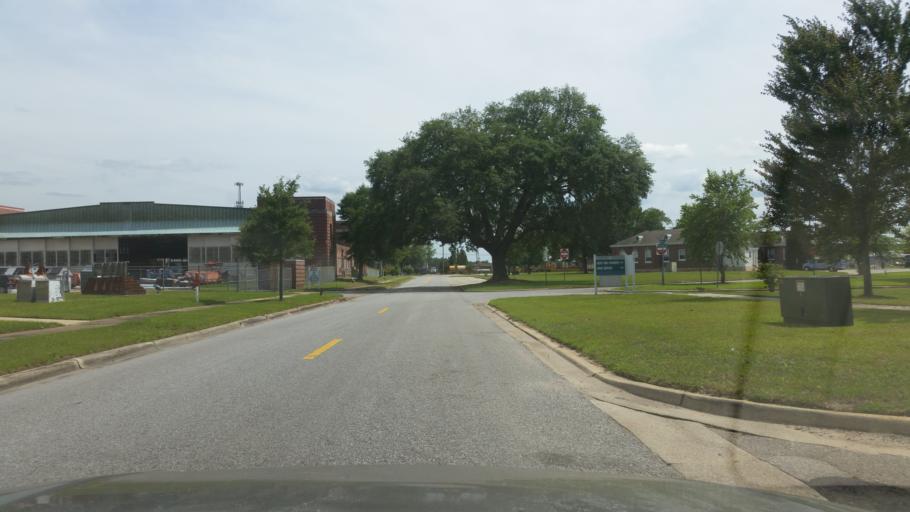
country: US
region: Florida
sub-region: Escambia County
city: Ferry Pass
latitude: 30.5296
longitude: -87.1987
